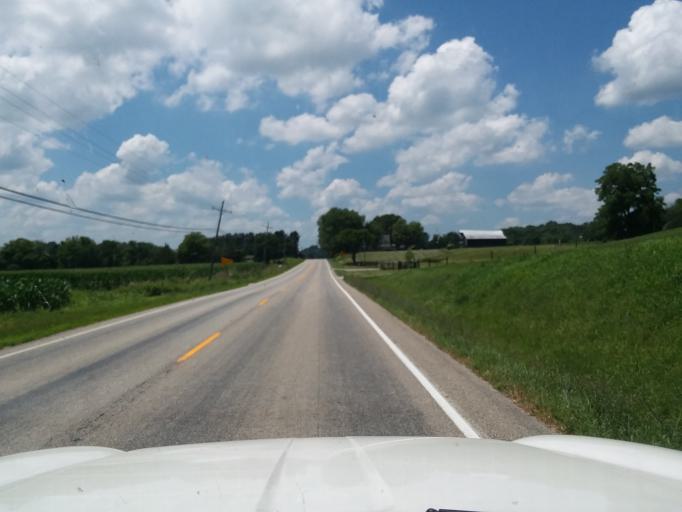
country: US
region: Indiana
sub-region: Johnson County
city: Trafalgar
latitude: 39.3719
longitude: -86.2884
